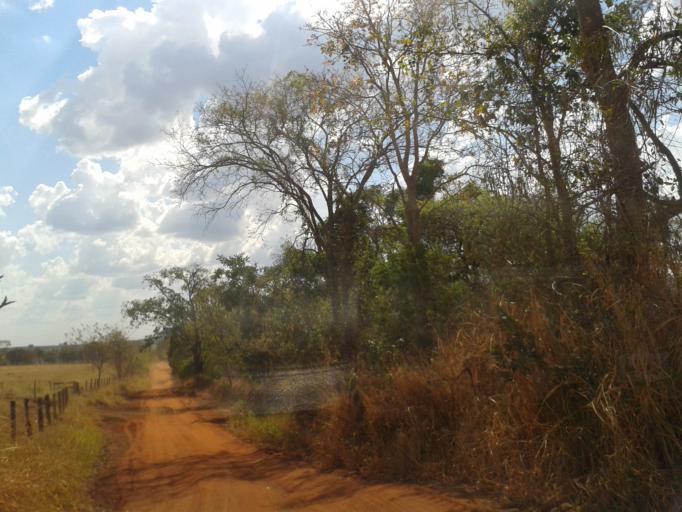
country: BR
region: Minas Gerais
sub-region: Santa Vitoria
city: Santa Vitoria
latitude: -19.1998
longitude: -49.9067
